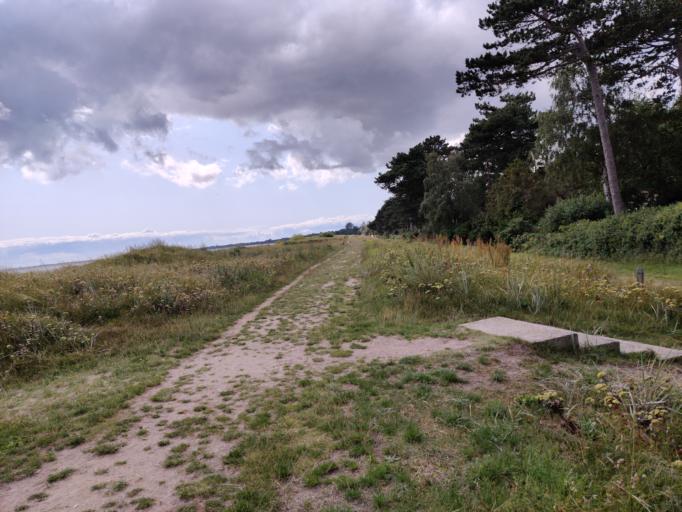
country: DK
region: Zealand
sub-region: Guldborgsund Kommune
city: Nykobing Falster
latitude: 54.7127
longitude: 11.9942
